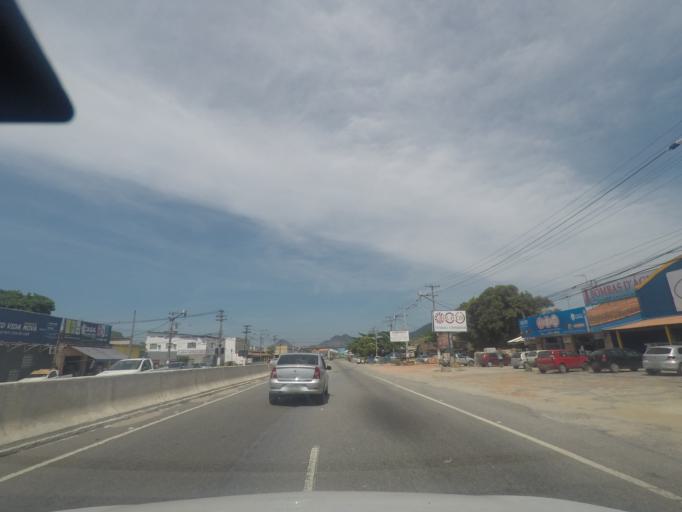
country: BR
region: Rio de Janeiro
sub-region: Marica
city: Marica
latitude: -22.9074
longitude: -42.8209
